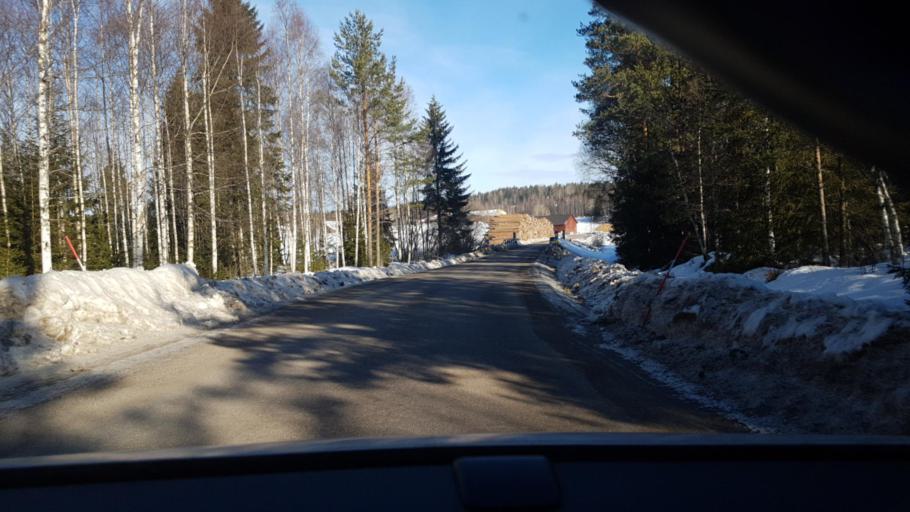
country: SE
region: Vaermland
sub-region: Eda Kommun
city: Charlottenberg
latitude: 59.8118
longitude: 12.1633
